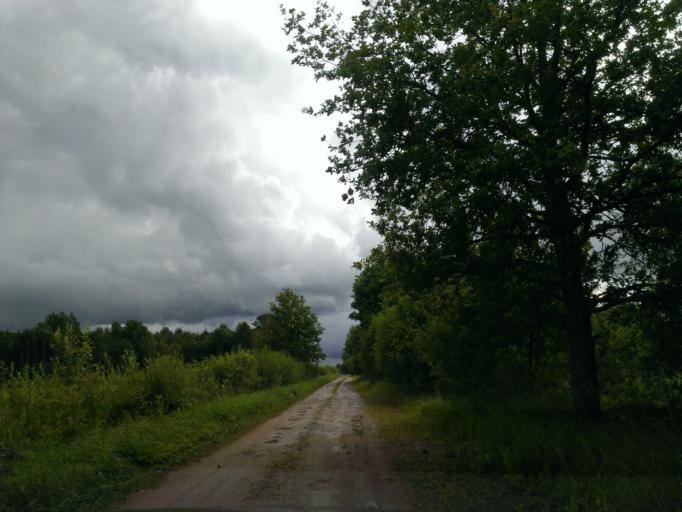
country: LV
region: Sigulda
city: Sigulda
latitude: 57.2153
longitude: 24.9386
